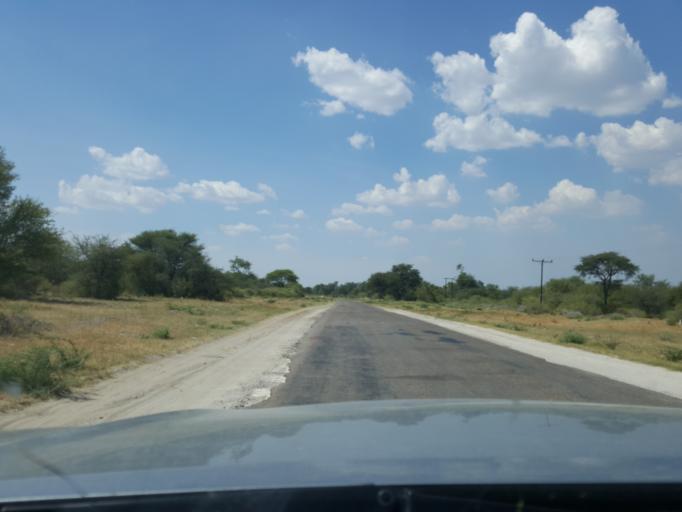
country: BW
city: Nokaneng
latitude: -19.4374
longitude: 22.1311
